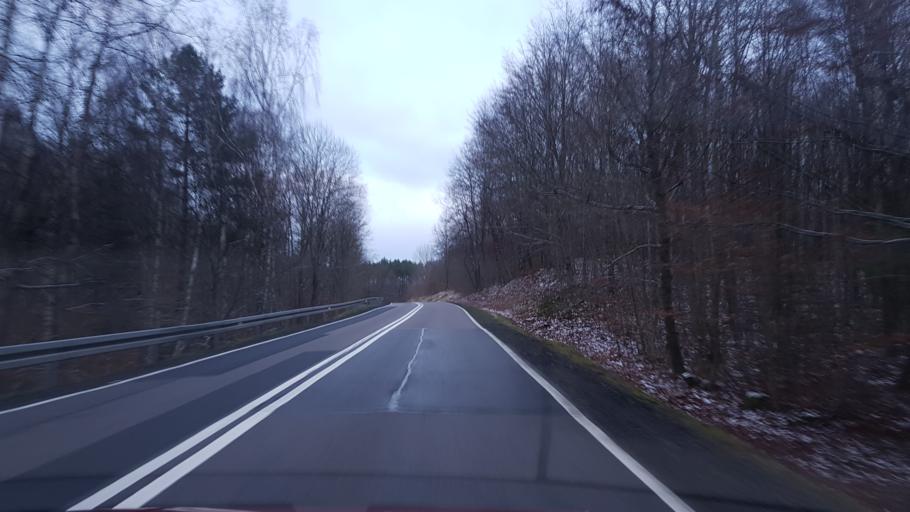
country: PL
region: Pomeranian Voivodeship
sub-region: Powiat bytowski
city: Tuchomie
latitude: 54.0666
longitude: 17.2703
